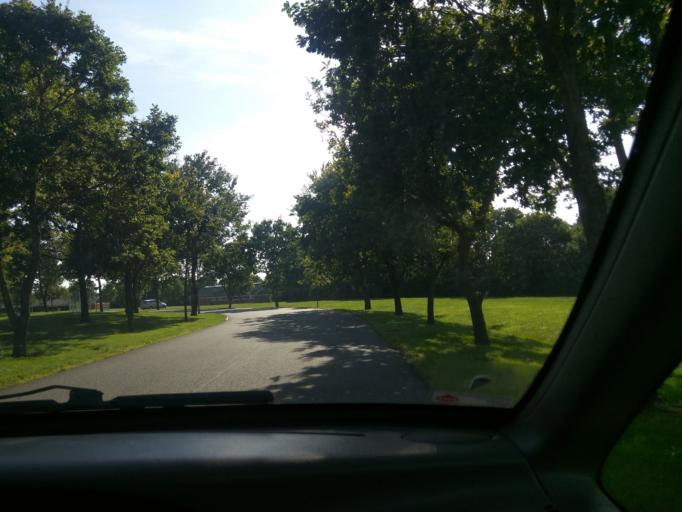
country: DK
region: Central Jutland
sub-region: Viborg Kommune
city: Bjerringbro
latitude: 56.4901
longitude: 9.5819
